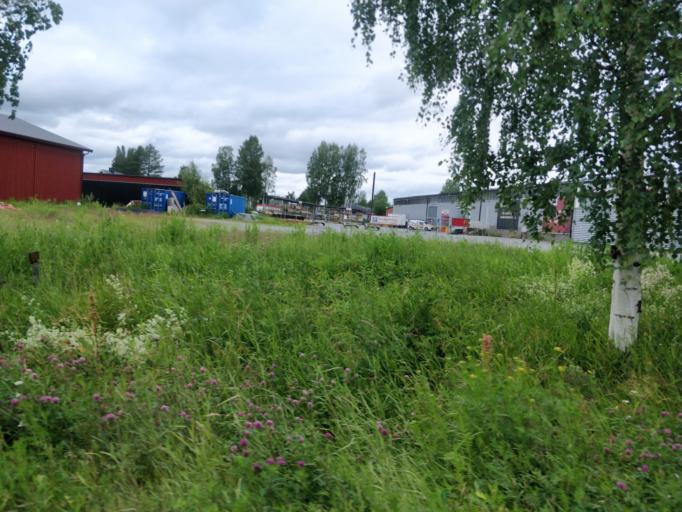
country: SE
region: Vaesterbotten
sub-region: Skelleftea Kommun
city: Viken
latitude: 64.7588
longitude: 20.8901
